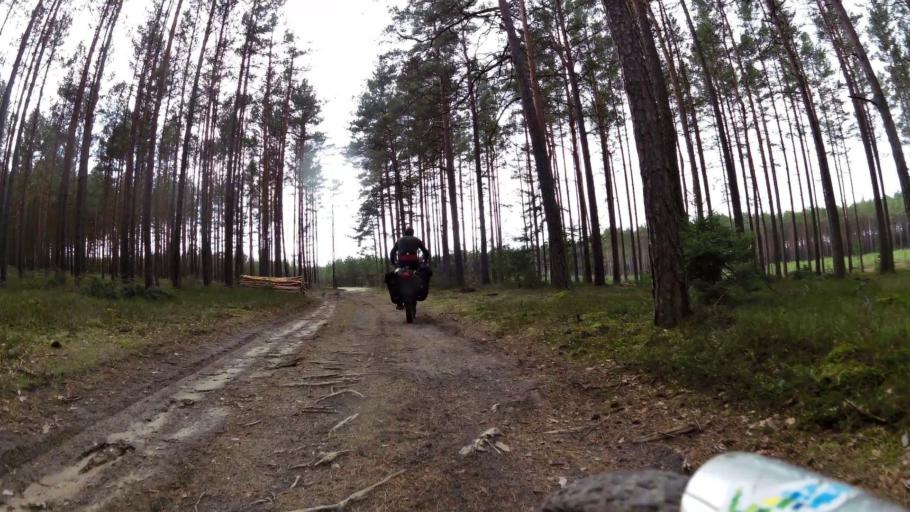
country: PL
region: Pomeranian Voivodeship
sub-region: Powiat bytowski
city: Kolczyglowy
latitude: 54.1648
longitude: 17.1937
